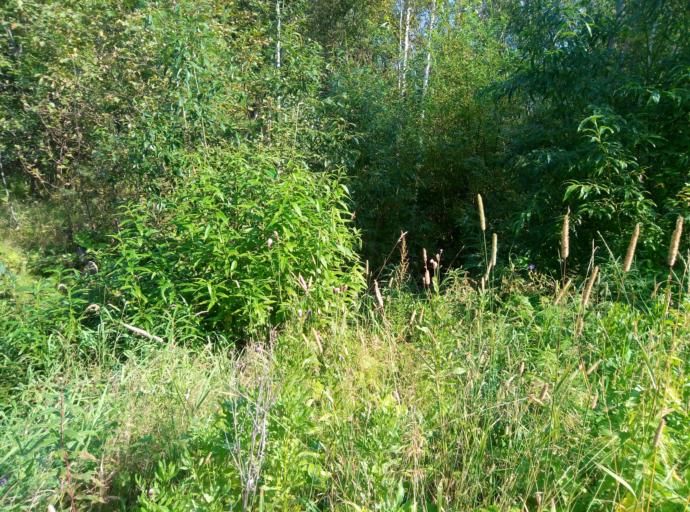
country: RU
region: Sverdlovsk
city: Rudnichnyy
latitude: 59.7286
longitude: 60.3286
